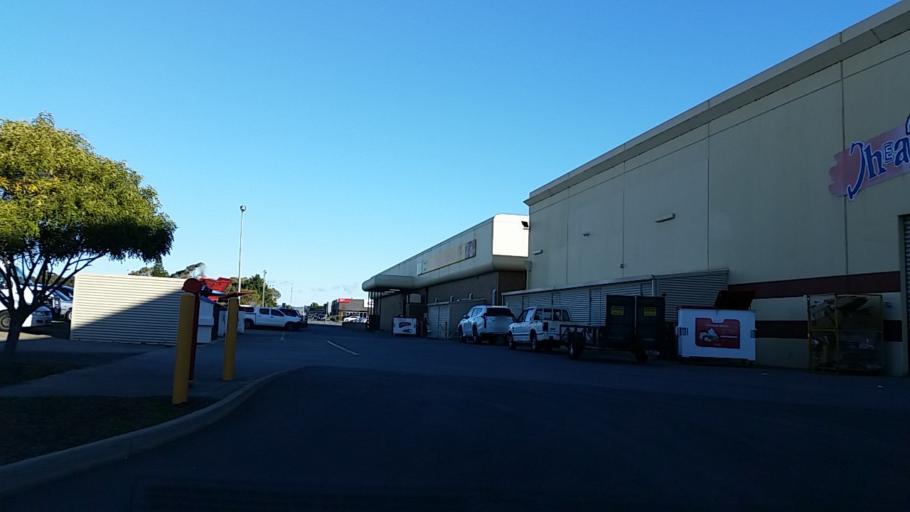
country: AU
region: South Australia
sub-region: Onkaparinga
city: Seaford
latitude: -35.1892
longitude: 138.4799
